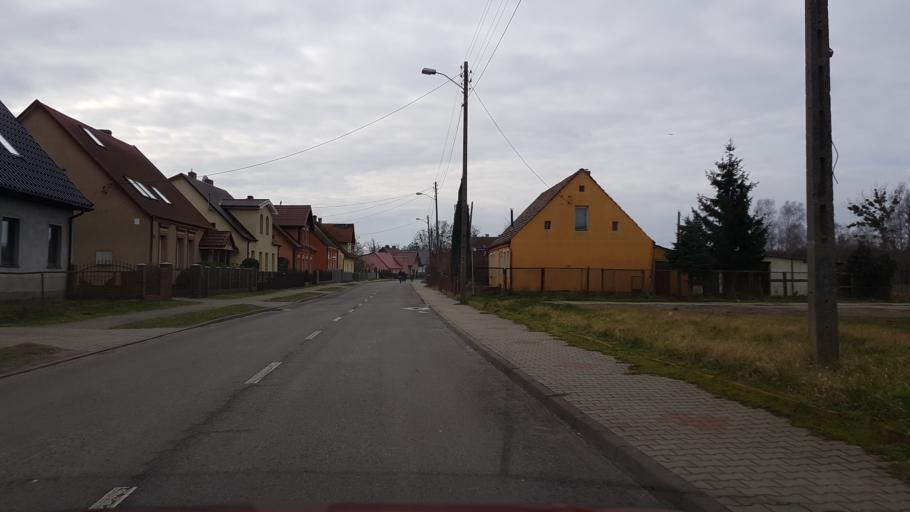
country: PL
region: West Pomeranian Voivodeship
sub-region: Powiat goleniowski
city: Stepnica
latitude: 53.6552
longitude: 14.5048
